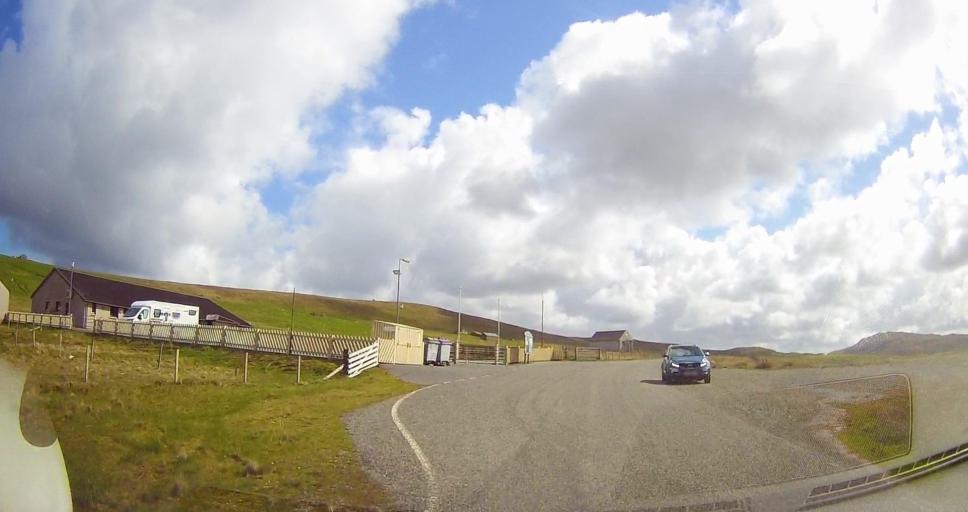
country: GB
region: Scotland
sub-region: Shetland Islands
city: Lerwick
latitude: 60.5716
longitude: -1.3326
